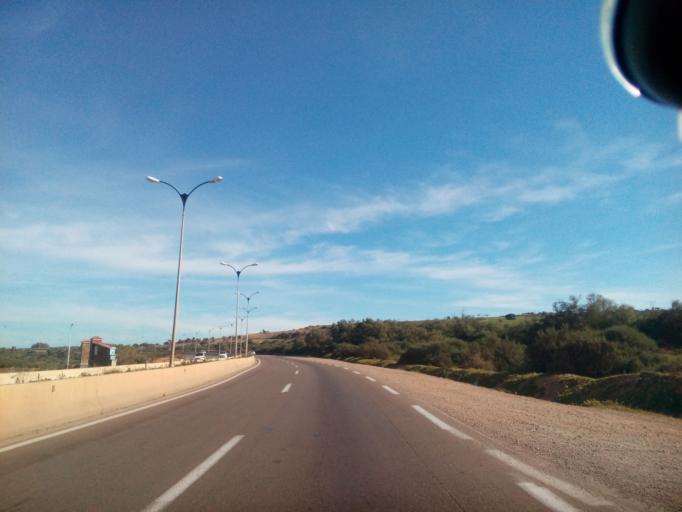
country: DZ
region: Oran
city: Ain el Bya
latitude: 35.7885
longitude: -0.0977
